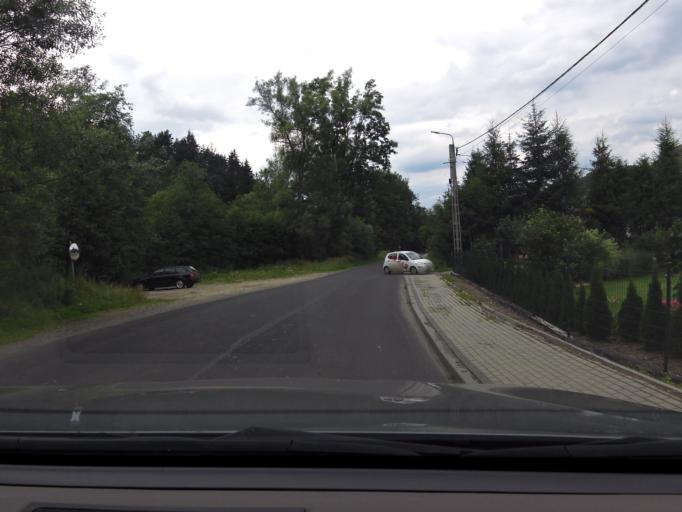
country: PL
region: Silesian Voivodeship
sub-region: Powiat zywiecki
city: Ujsoly
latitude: 49.4858
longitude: 19.1270
